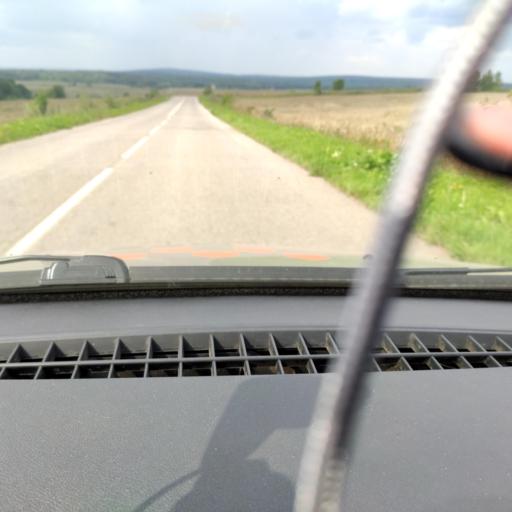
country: RU
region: Bashkortostan
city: Iglino
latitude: 54.7714
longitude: 56.5512
